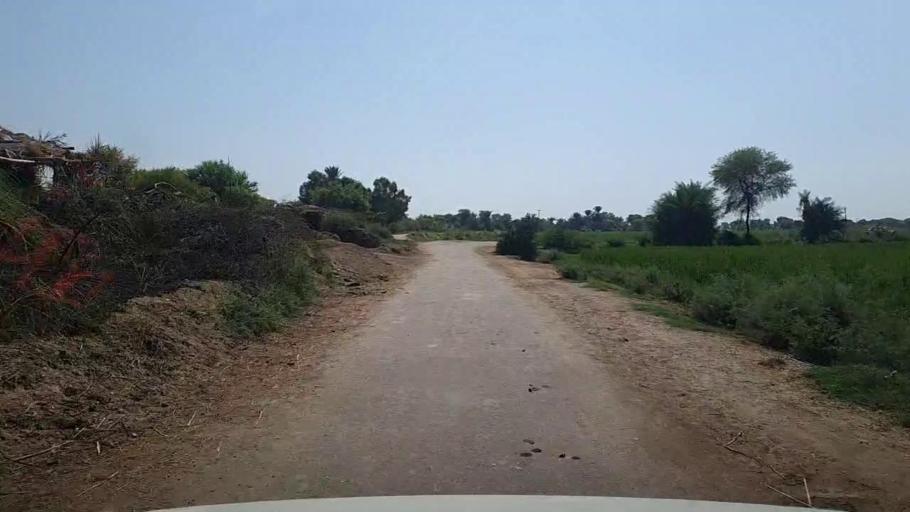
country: PK
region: Sindh
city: Kandhkot
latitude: 28.3225
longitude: 69.3360
